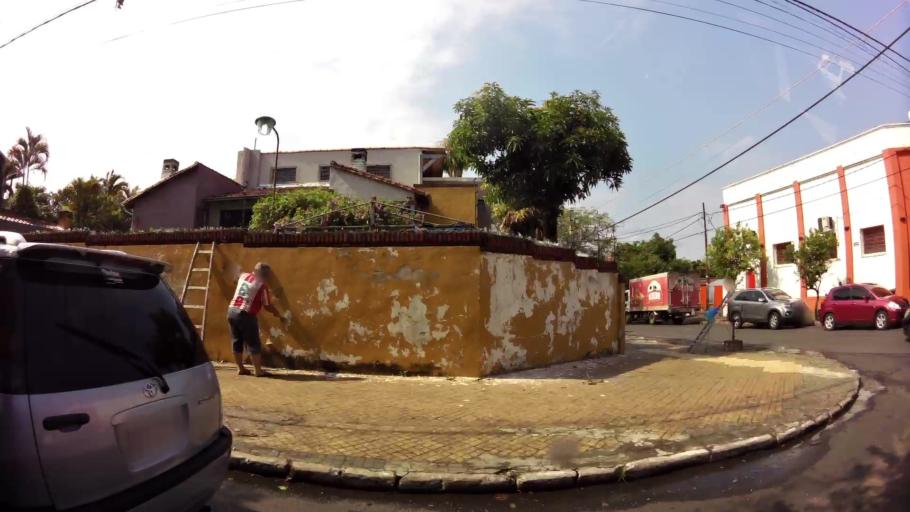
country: PY
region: Presidente Hayes
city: Nanawa
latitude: -25.2915
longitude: -57.6646
